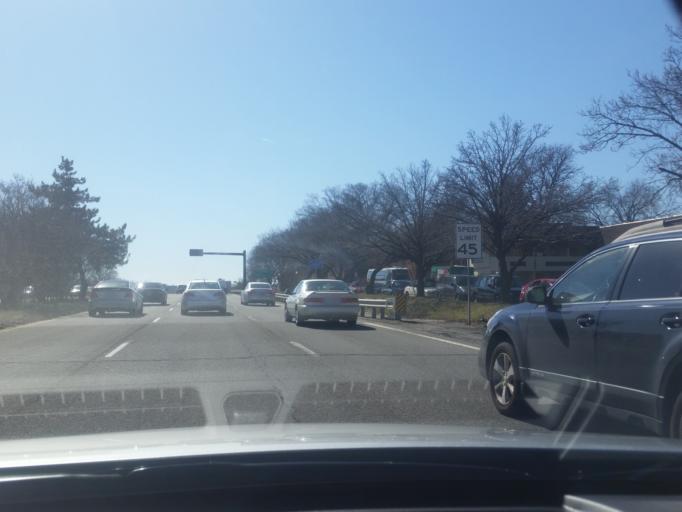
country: US
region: Virginia
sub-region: Arlington County
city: Arlington
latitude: 38.8808
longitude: -77.0842
